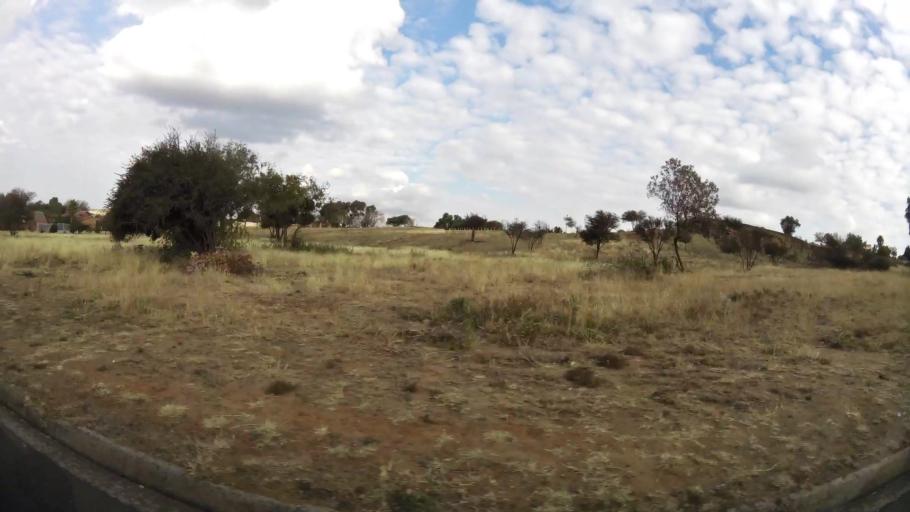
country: ZA
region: Orange Free State
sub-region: Mangaung Metropolitan Municipality
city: Bloemfontein
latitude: -29.0813
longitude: 26.2041
